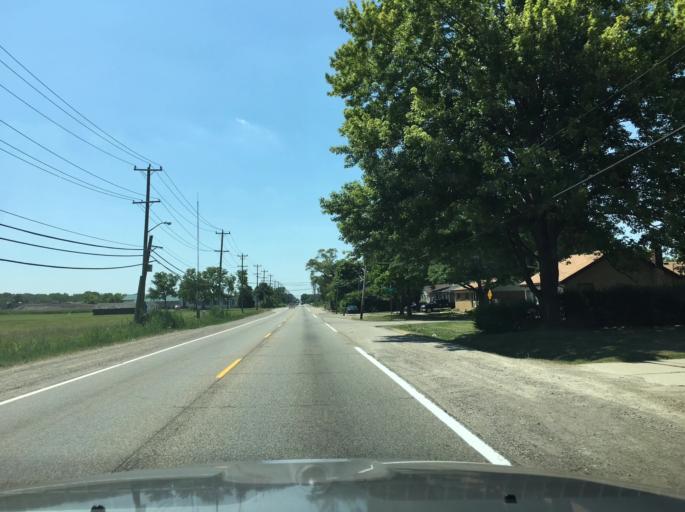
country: US
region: Michigan
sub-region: Macomb County
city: Mount Clemens
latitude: 42.5552
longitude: -82.8751
